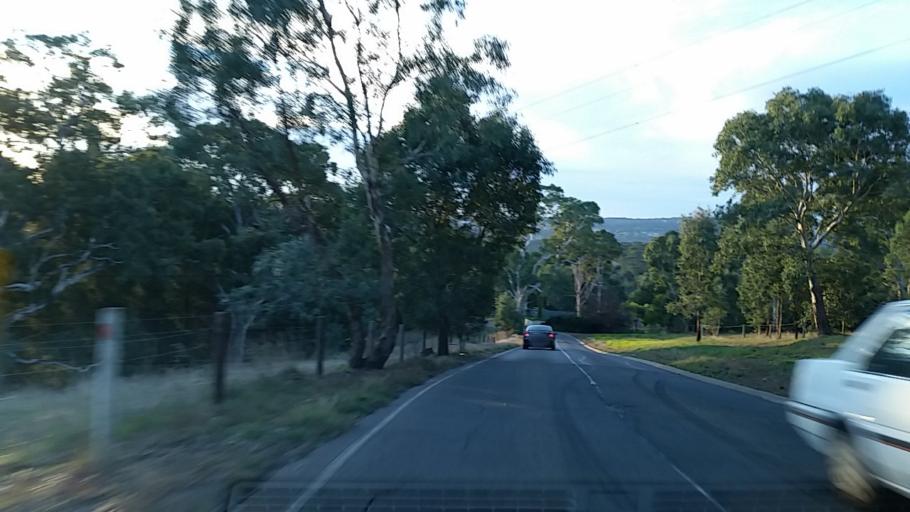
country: AU
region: South Australia
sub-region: Onkaparinga
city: Craigburn Farm
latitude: -35.0722
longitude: 138.6189
